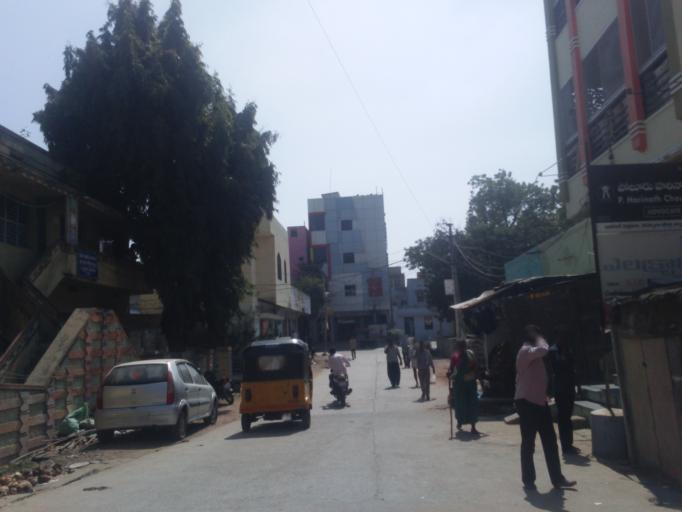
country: IN
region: Telangana
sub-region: Mahbubnagar
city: Alampur
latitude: 15.8232
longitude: 78.0411
